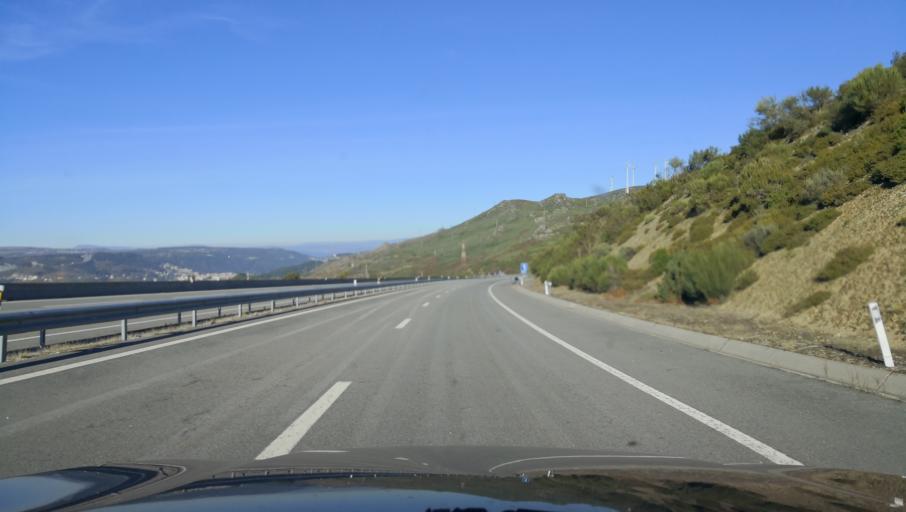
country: PT
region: Vila Real
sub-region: Vila Pouca de Aguiar
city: Vila Pouca de Aguiar
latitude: 41.4496
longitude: -7.6472
